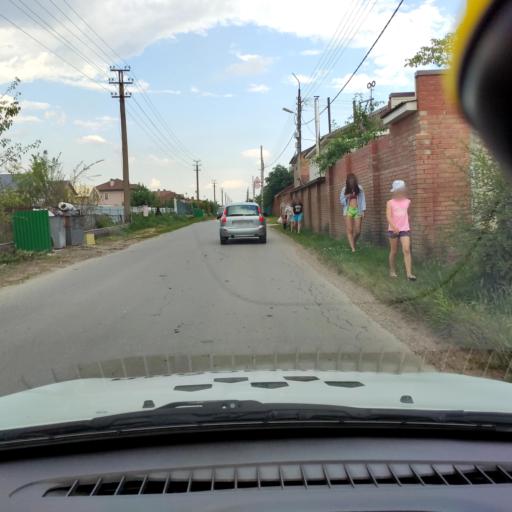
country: RU
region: Samara
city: Podstepki
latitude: 53.5086
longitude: 49.1745
